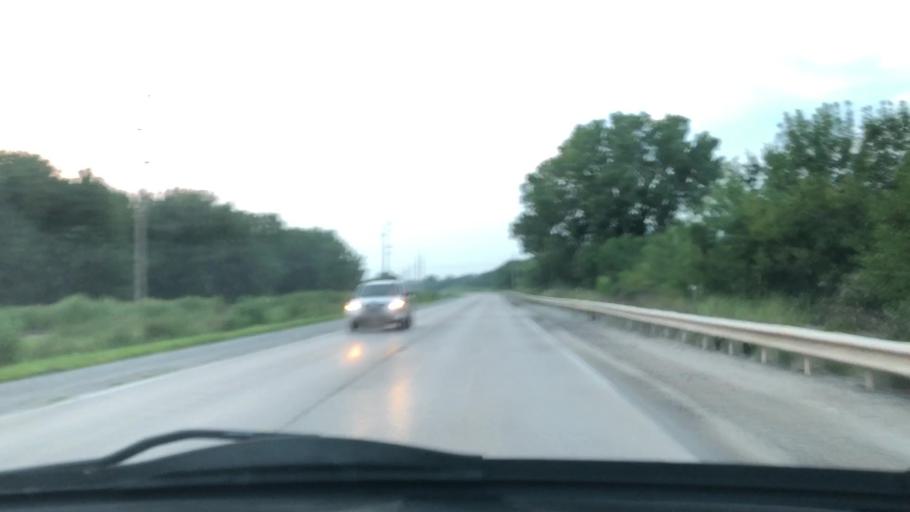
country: US
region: Iowa
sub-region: Johnson County
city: North Liberty
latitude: 41.7926
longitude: -91.6401
